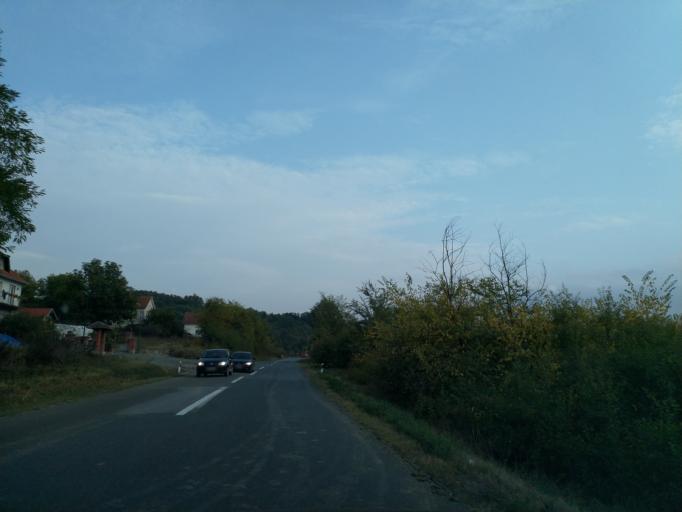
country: RS
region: Central Serbia
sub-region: Sumadijski Okrug
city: Topola
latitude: 44.2224
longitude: 20.7182
